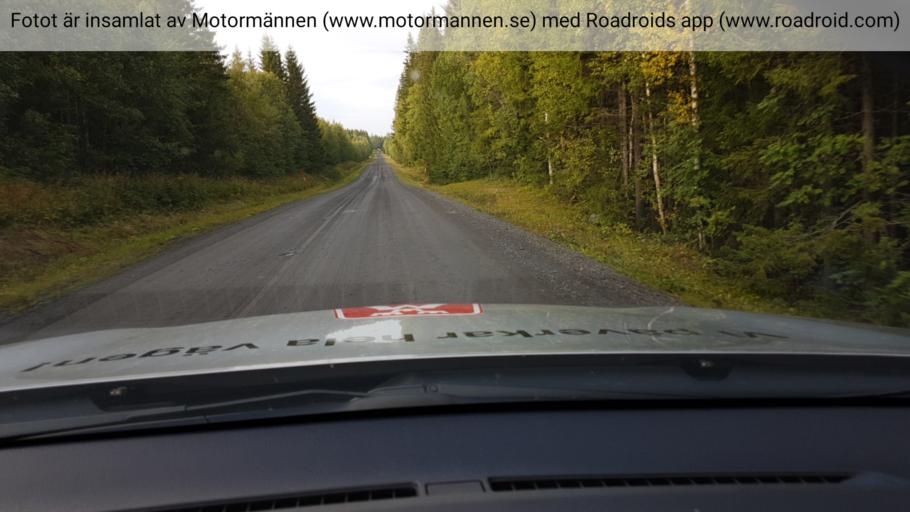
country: SE
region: Jaemtland
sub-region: Stroemsunds Kommun
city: Stroemsund
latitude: 64.1020
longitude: 15.8235
